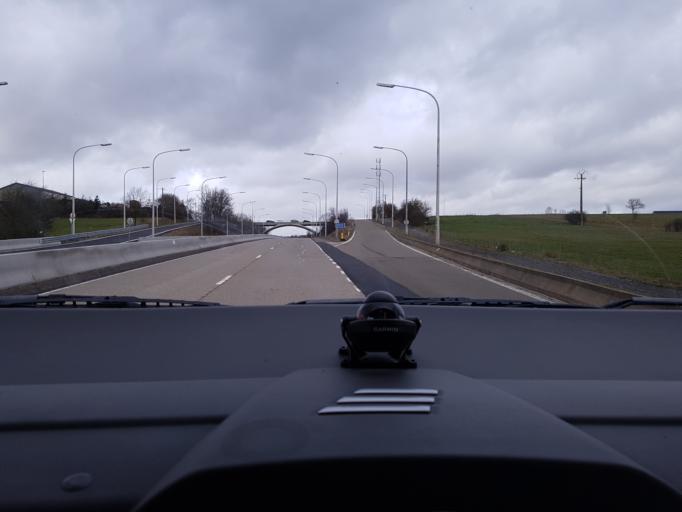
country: BE
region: Wallonia
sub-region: Province de Namur
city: Hamois
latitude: 50.2737
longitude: 5.2384
